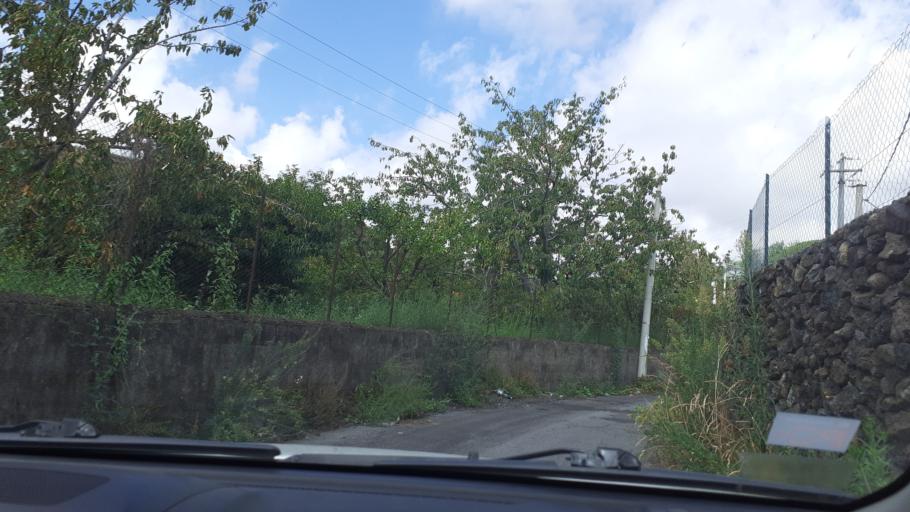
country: IT
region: Sicily
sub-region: Catania
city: Trecastagni
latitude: 37.5975
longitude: 15.0767
